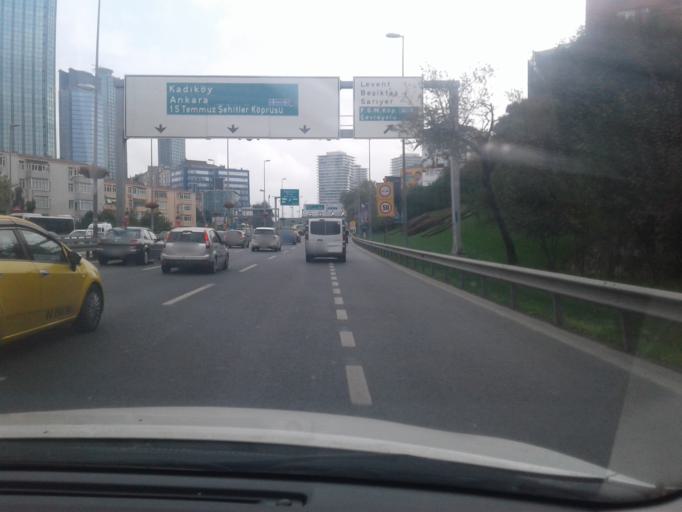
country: TR
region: Istanbul
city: Sisli
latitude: 41.0668
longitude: 29.0066
